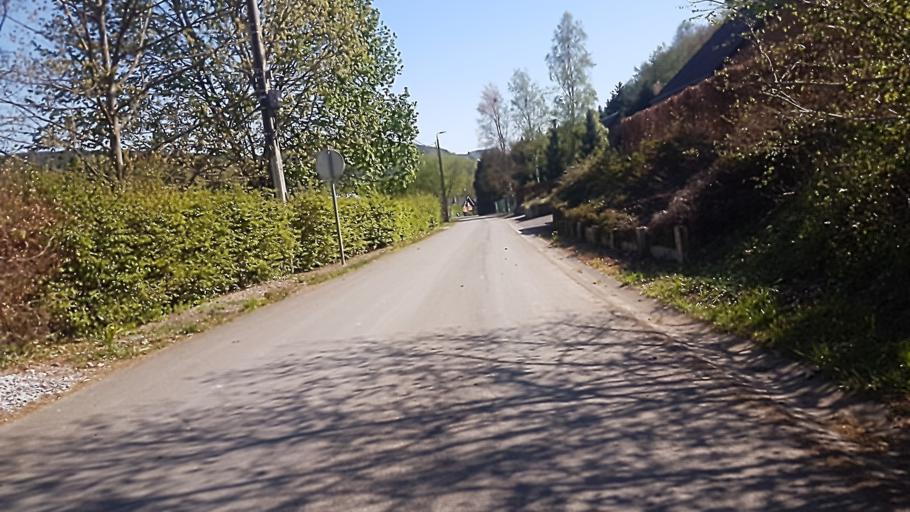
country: BE
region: Wallonia
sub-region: Province de Namur
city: Couvin
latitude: 50.0710
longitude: 4.6005
